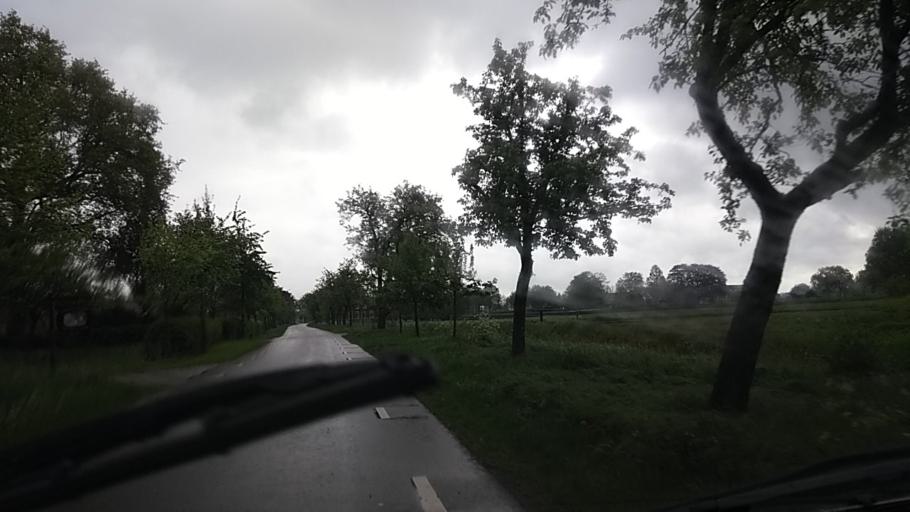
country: NL
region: Drenthe
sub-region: Gemeente Westerveld
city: Havelte
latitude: 52.7464
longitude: 6.2907
